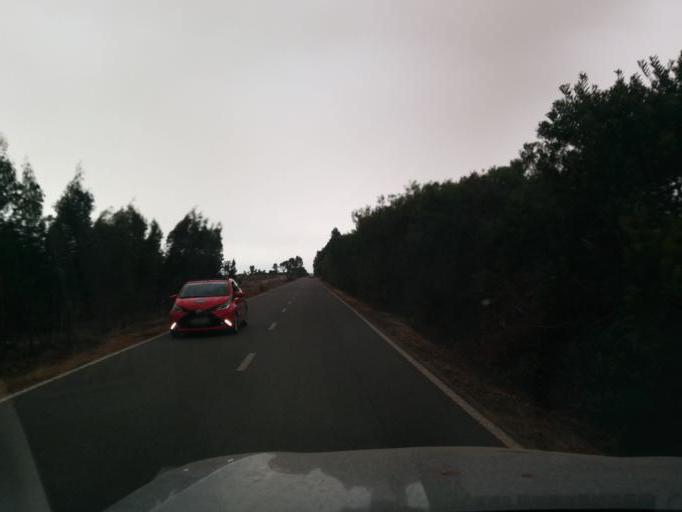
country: PT
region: Beja
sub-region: Odemira
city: Sao Teotonio
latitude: 37.5397
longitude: -8.7509
